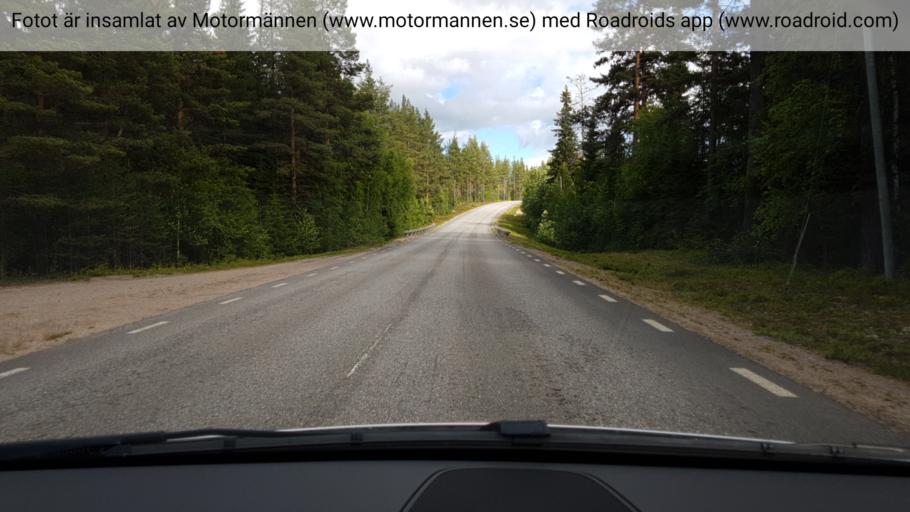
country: SE
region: Jaemtland
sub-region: Harjedalens Kommun
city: Sveg
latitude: 62.0134
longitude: 14.8793
